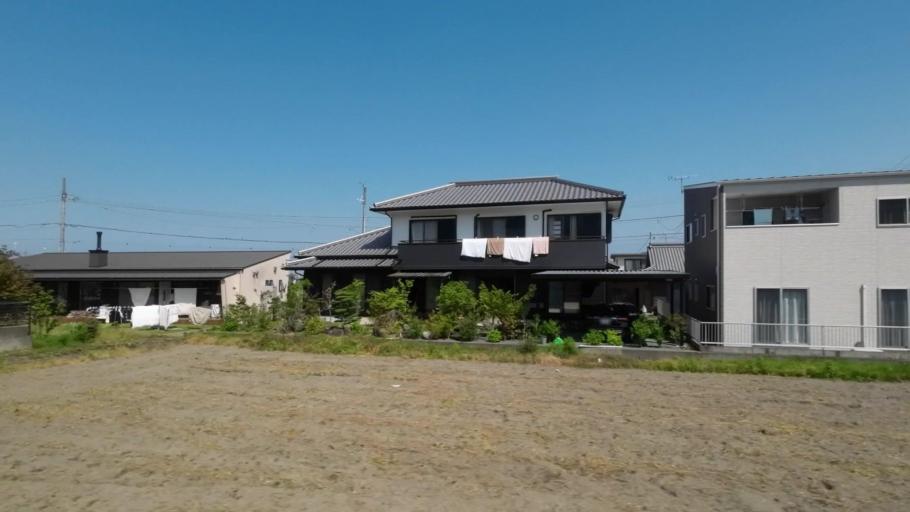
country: JP
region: Ehime
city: Kawanoecho
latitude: 33.9699
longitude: 133.5178
